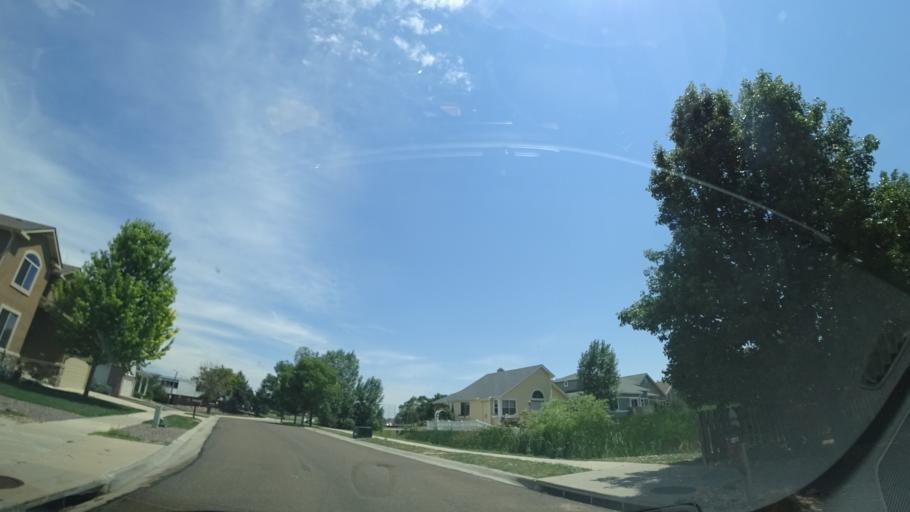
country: US
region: Colorado
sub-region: Jefferson County
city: Lakewood
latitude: 39.6936
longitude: -105.0872
